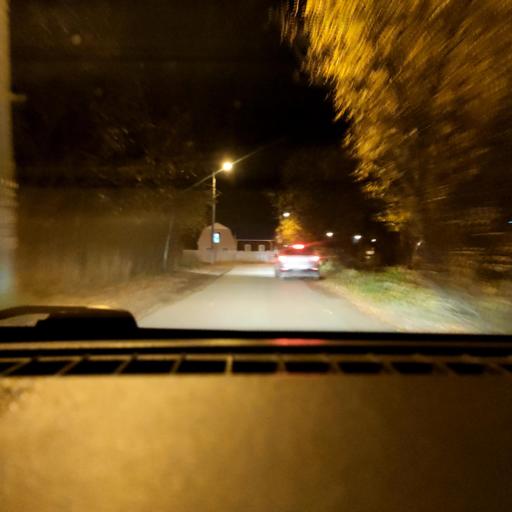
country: RU
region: Perm
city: Perm
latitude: 58.0378
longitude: 56.3530
